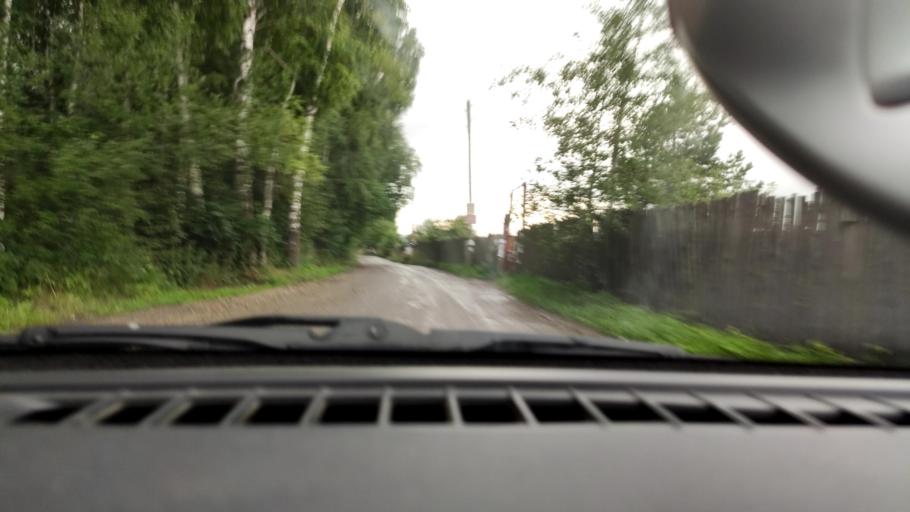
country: RU
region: Perm
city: Overyata
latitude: 58.0522
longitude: 55.9898
